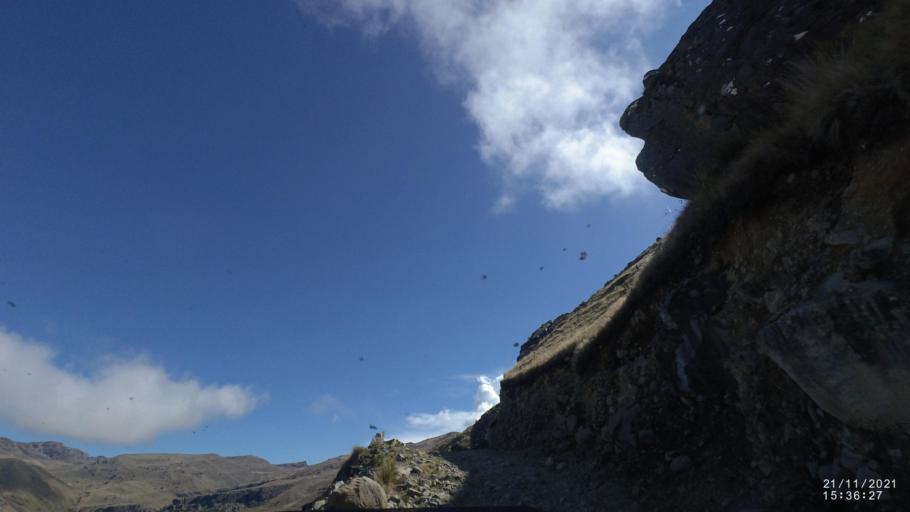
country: BO
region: Cochabamba
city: Cochabamba
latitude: -16.9611
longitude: -66.2664
